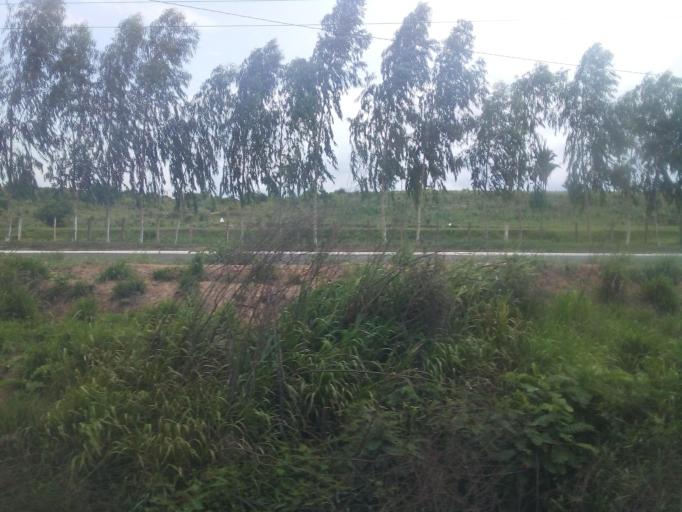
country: BR
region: Maranhao
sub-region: Santa Ines
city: Santa Ines
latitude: -3.7015
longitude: -45.9677
